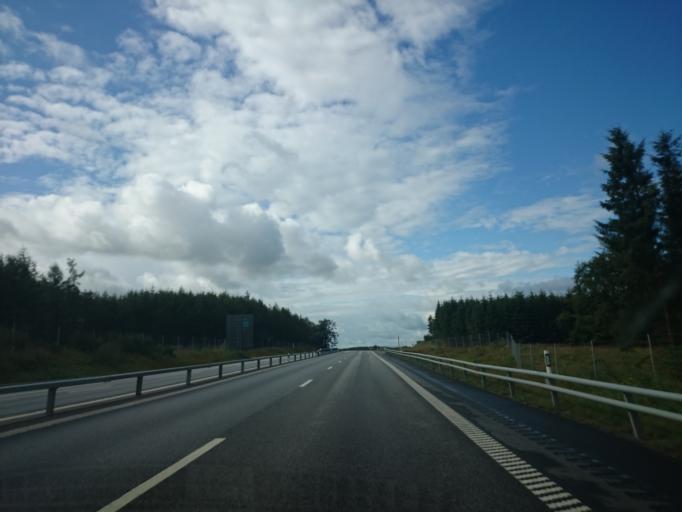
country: SE
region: Skane
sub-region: Horby Kommun
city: Hoerby
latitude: 55.8809
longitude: 13.7133
